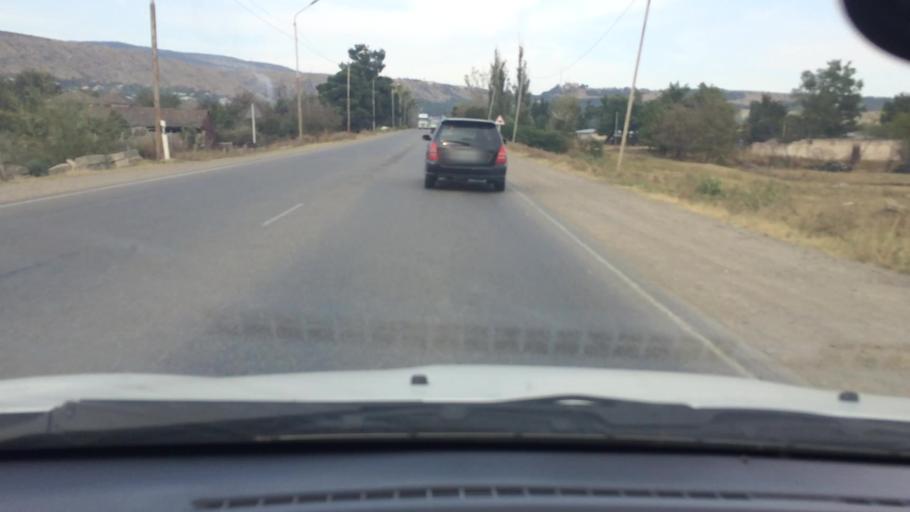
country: GE
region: T'bilisi
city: Tbilisi
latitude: 41.6080
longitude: 44.7843
